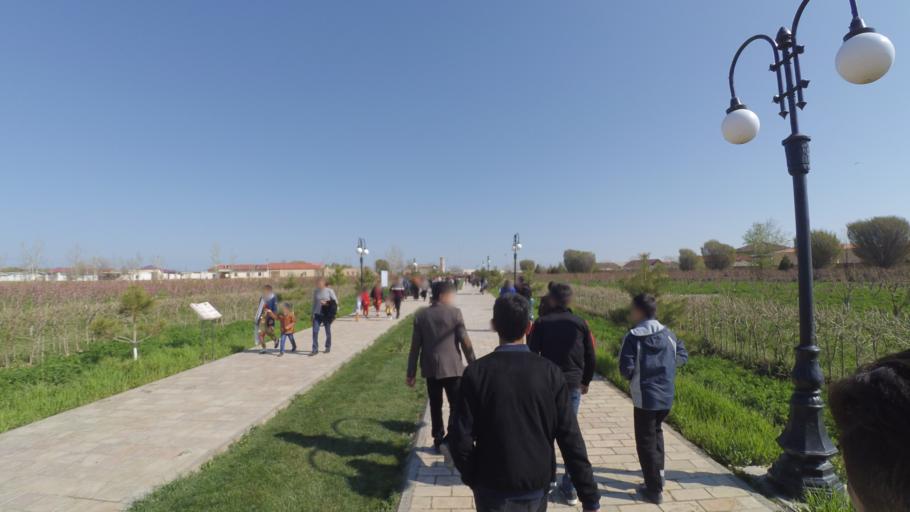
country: UZ
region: Bukhara
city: Kogon
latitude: 39.8034
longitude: 64.5392
